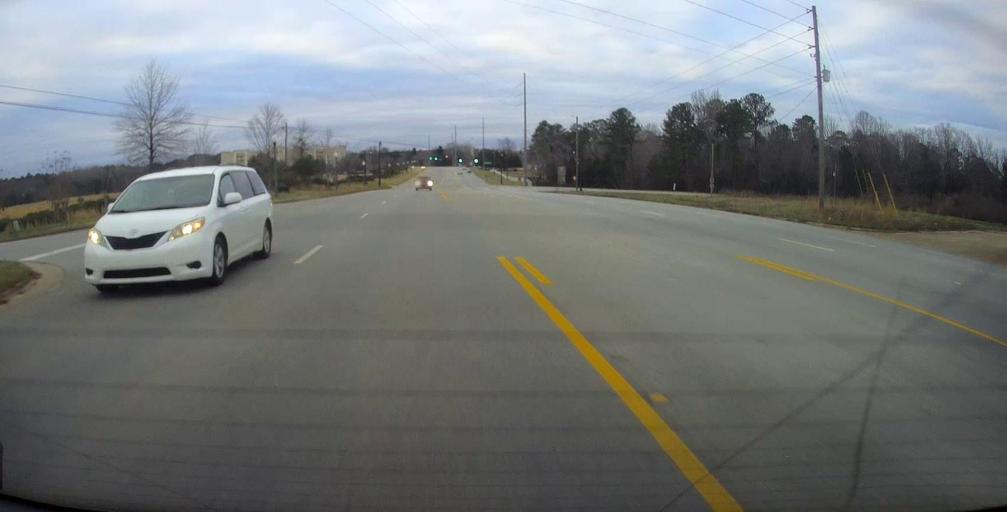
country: US
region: Alabama
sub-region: Chambers County
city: Huguley
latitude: 32.8239
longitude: -85.2154
